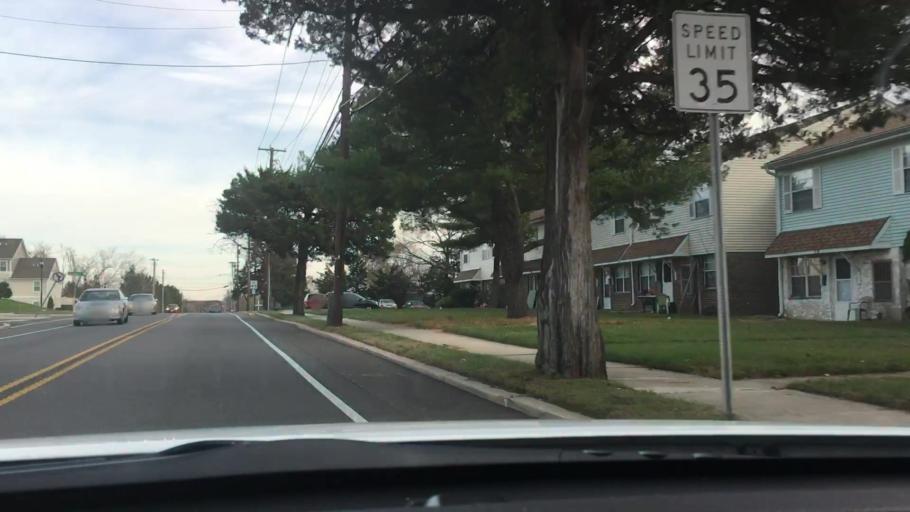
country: US
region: New Jersey
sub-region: Atlantic County
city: Absecon
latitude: 39.4152
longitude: -74.5121
